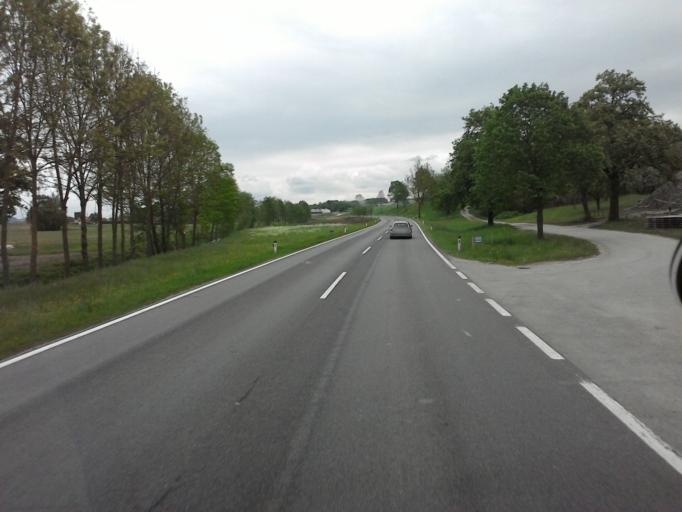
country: AT
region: Upper Austria
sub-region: Politischer Bezirk Grieskirchen
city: Grieskirchen
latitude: 48.2206
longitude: 13.7192
